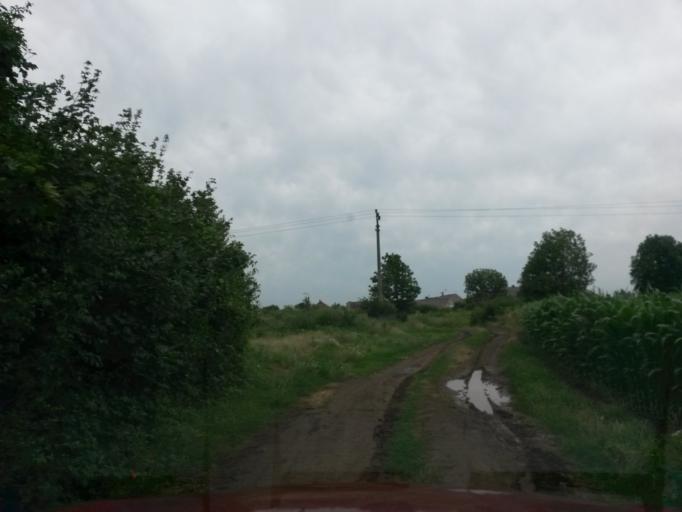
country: SK
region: Nitriansky
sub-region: Okres Nitra
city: Nitra
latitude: 48.3408
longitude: 17.9881
